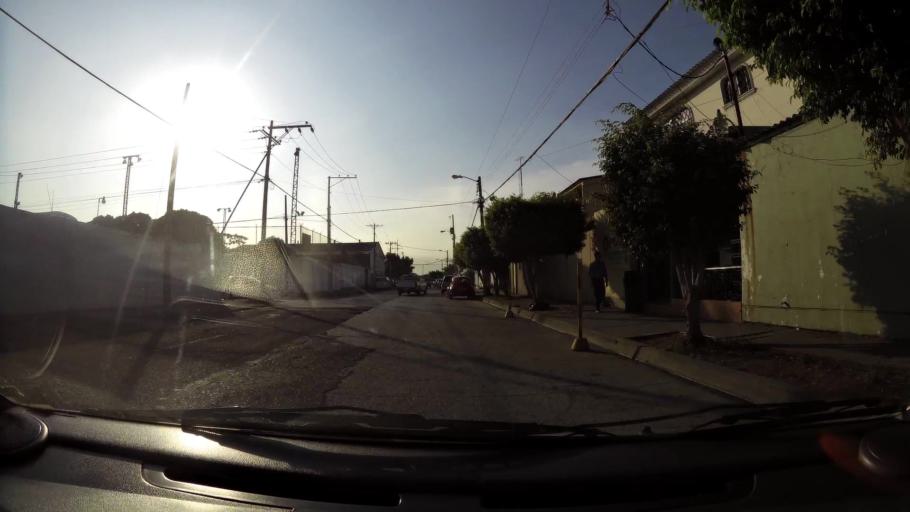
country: EC
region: Guayas
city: Eloy Alfaro
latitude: -2.1692
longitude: -79.8934
